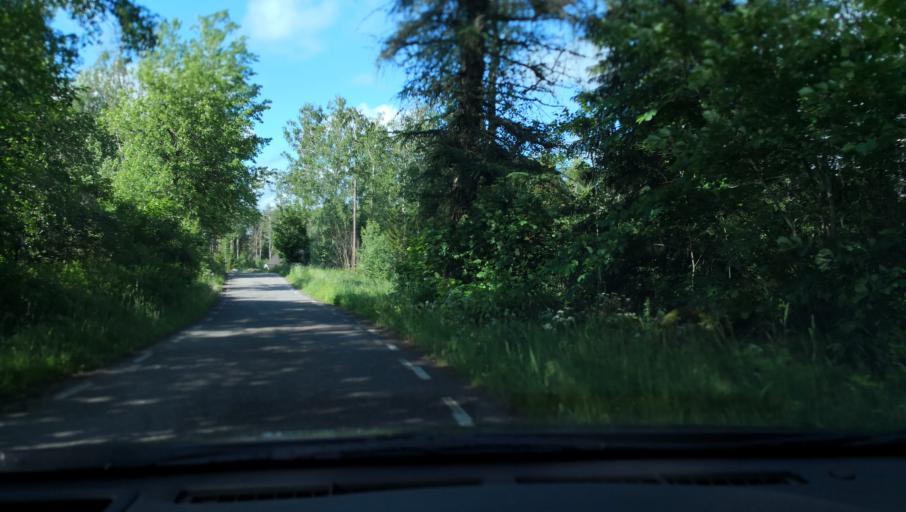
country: SE
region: OErebro
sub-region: Lindesbergs Kommun
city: Fellingsbro
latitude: 59.3311
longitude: 15.6863
